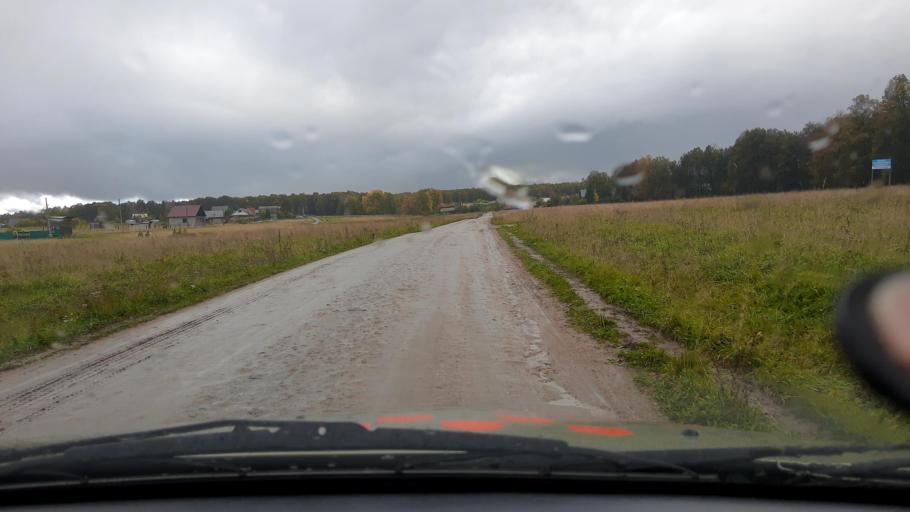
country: RU
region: Bashkortostan
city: Kudeyevskiy
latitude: 54.8789
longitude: 56.6308
